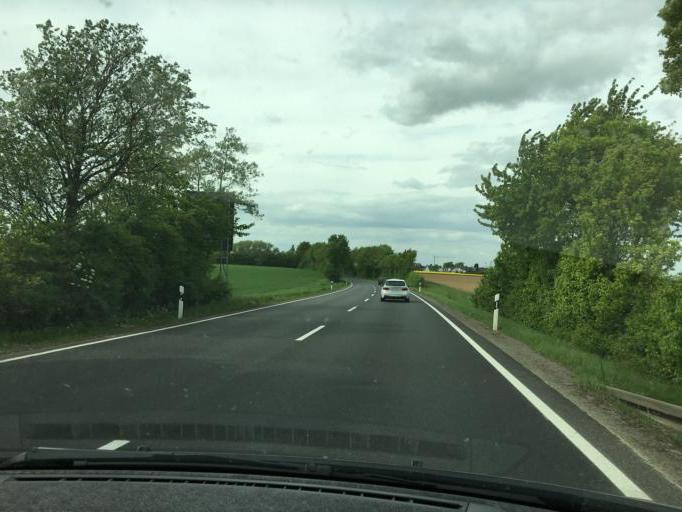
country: DE
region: North Rhine-Westphalia
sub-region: Regierungsbezirk Koln
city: Euskirchen
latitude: 50.6851
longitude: 6.7476
